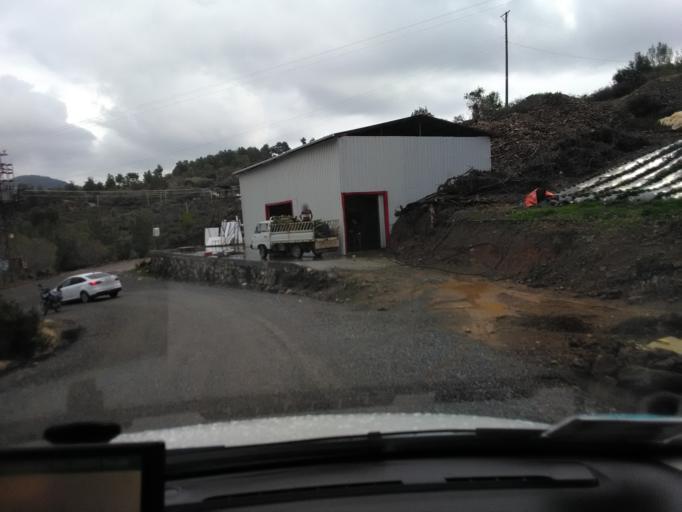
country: TR
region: Antalya
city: Gazipasa
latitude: 36.1602
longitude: 32.4321
